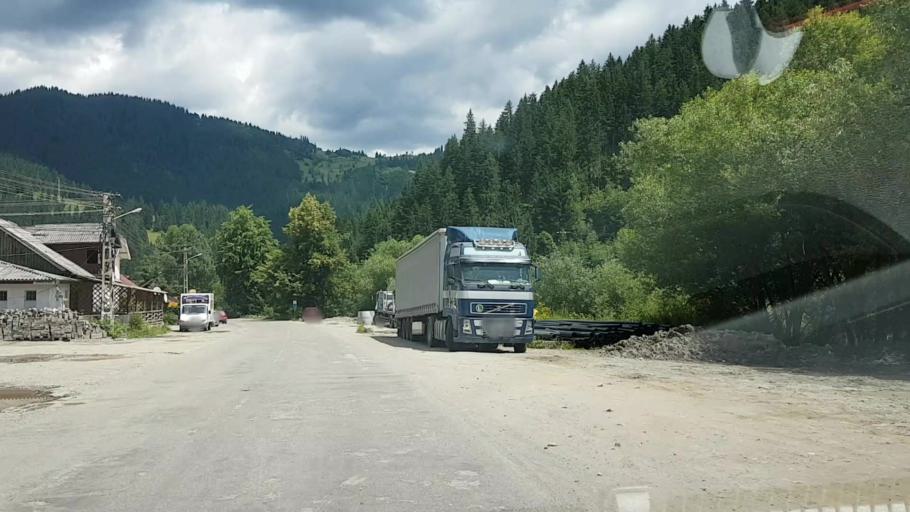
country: RO
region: Suceava
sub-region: Comuna Brosteni
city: Brosteni
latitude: 47.2377
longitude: 25.6964
